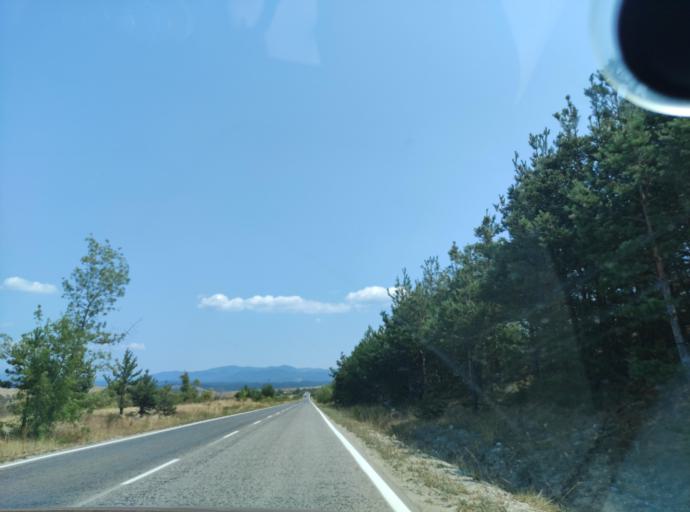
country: BG
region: Blagoevgrad
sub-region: Obshtina Razlog
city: Razlog
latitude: 41.8808
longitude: 23.4868
